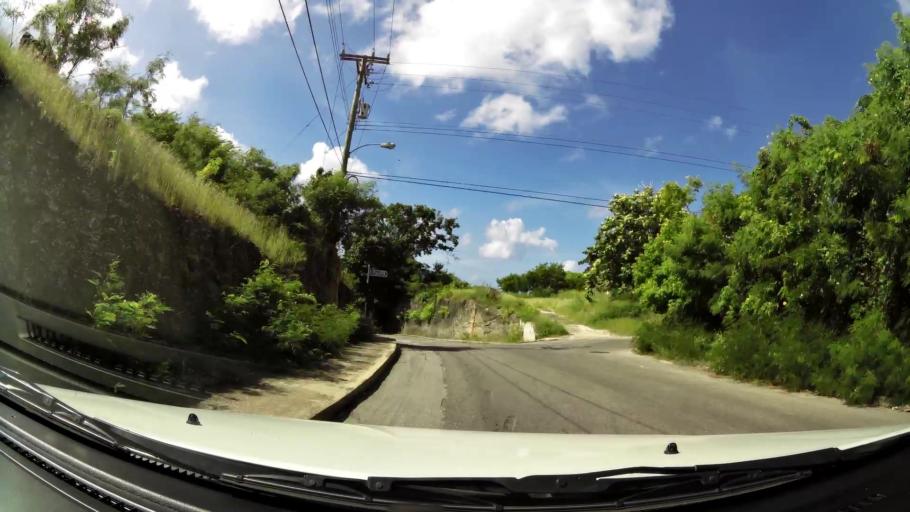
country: BB
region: Saint Peter
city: Speightstown
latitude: 13.2547
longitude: -59.6370
